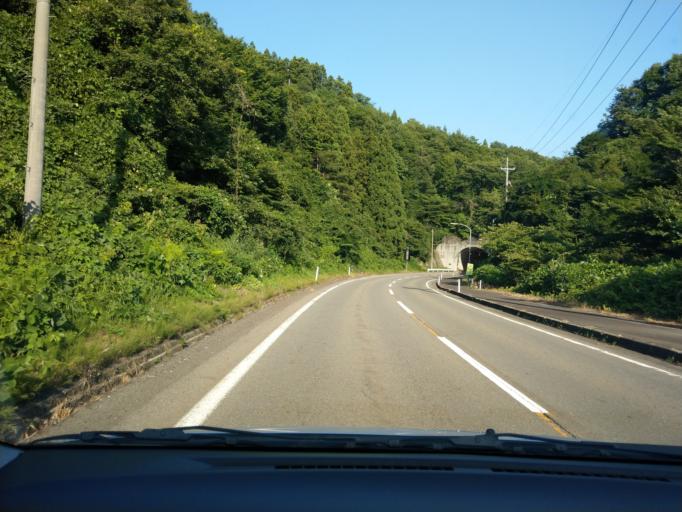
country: JP
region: Akita
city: Akita
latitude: 39.6066
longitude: 140.2052
